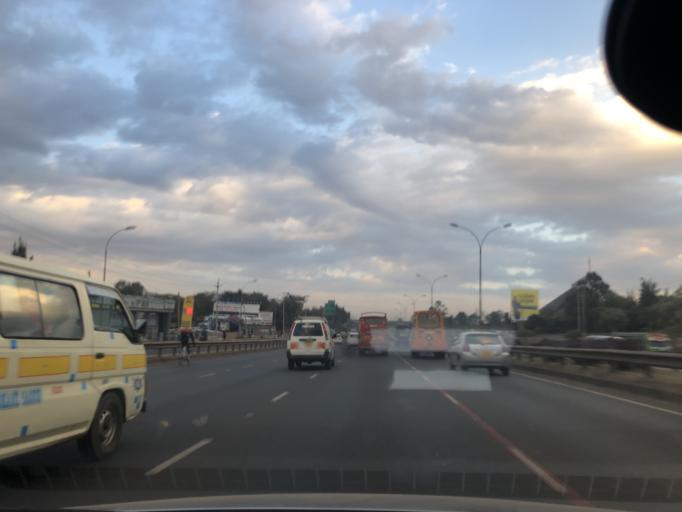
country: KE
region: Nairobi Area
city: Pumwani
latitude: -1.2285
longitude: 36.8810
